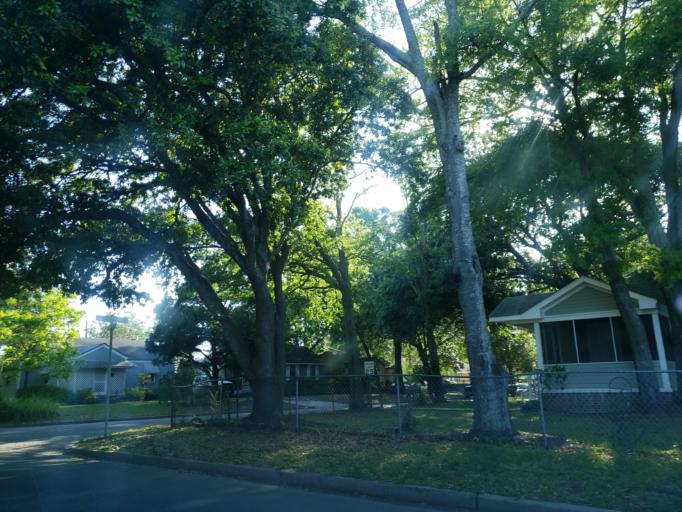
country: US
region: Georgia
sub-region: Chatham County
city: Thunderbolt
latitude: 32.0666
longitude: -81.0560
